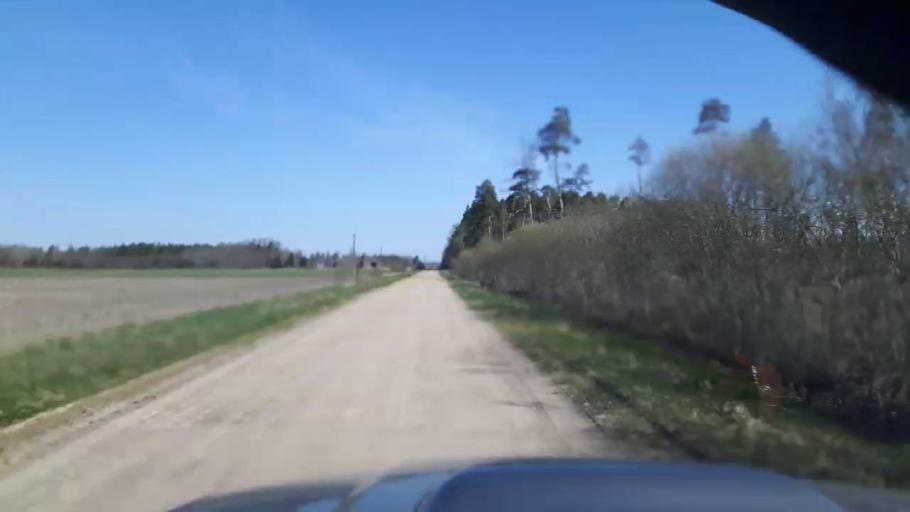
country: EE
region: Paernumaa
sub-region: Vaendra vald (alev)
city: Vandra
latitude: 58.5134
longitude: 24.9597
